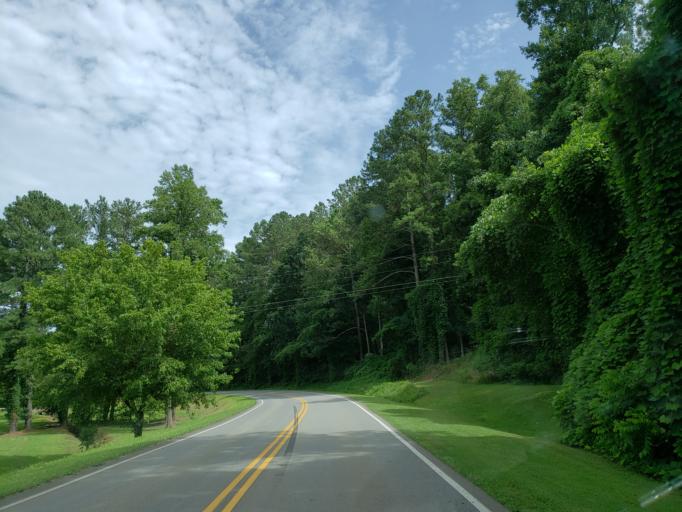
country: US
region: Georgia
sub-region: Pickens County
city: Jasper
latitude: 34.4487
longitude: -84.4381
